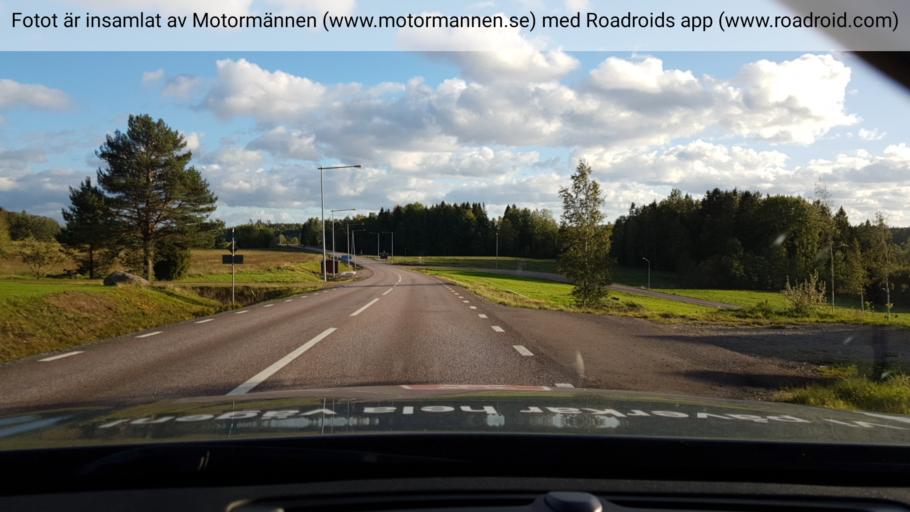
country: SE
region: Vaermland
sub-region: Karlstads Kommun
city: Molkom
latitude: 59.6423
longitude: 13.7158
